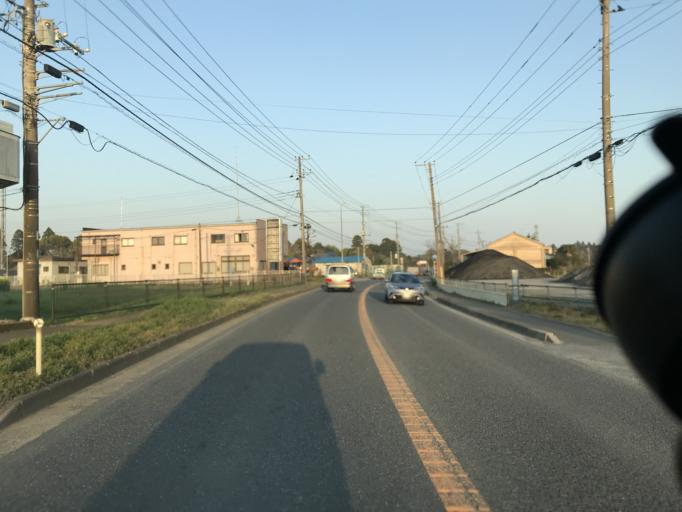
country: JP
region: Chiba
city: Narita
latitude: 35.8005
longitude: 140.3644
